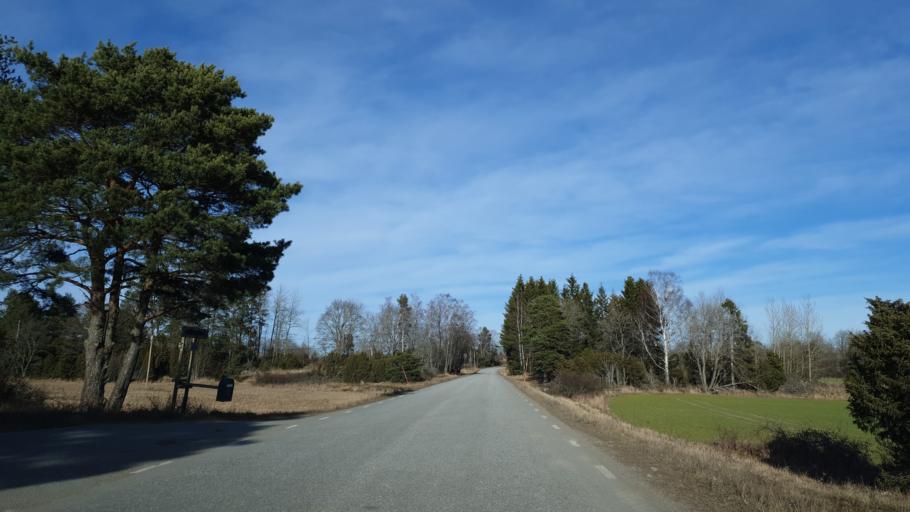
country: SE
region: Uppsala
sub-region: Enkopings Kommun
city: Grillby
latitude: 59.5541
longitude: 17.2343
